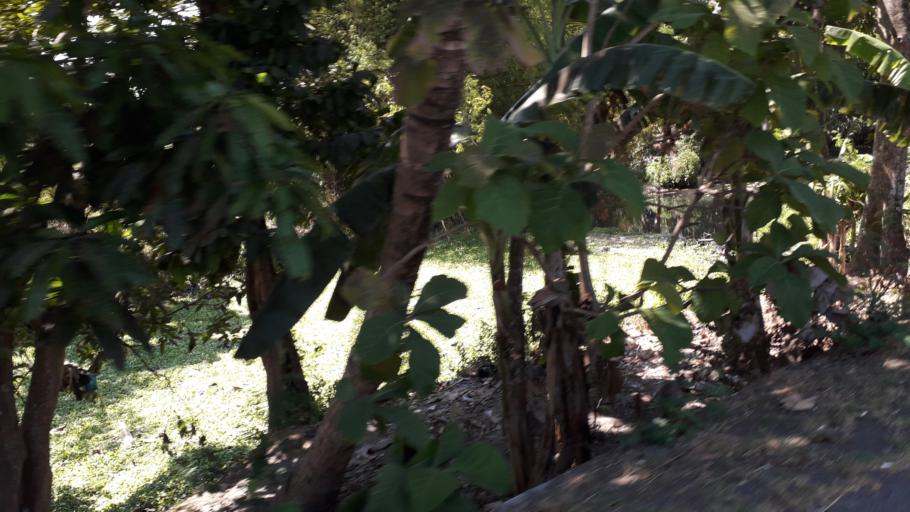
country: ID
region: Daerah Istimewa Yogyakarta
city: Pundong
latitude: -7.9461
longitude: 110.3295
